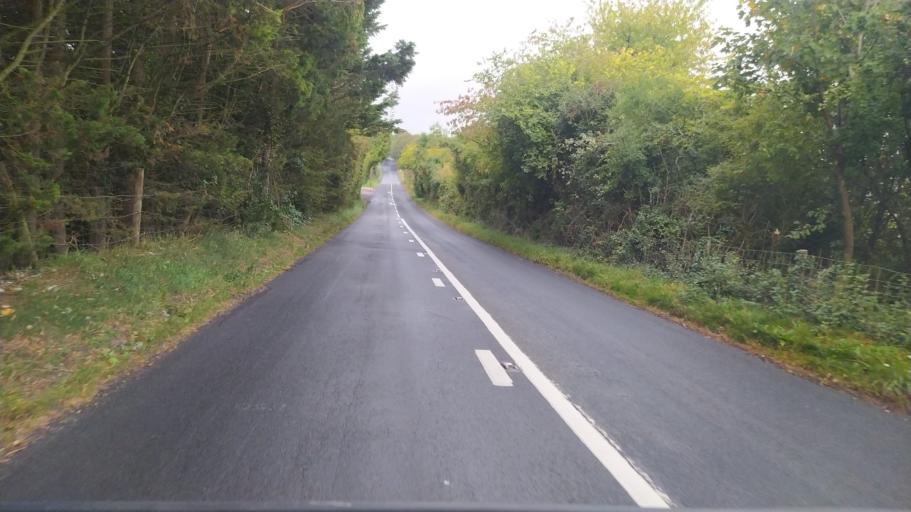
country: GB
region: England
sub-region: Wiltshire
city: Allington
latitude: 51.1164
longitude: -1.6292
